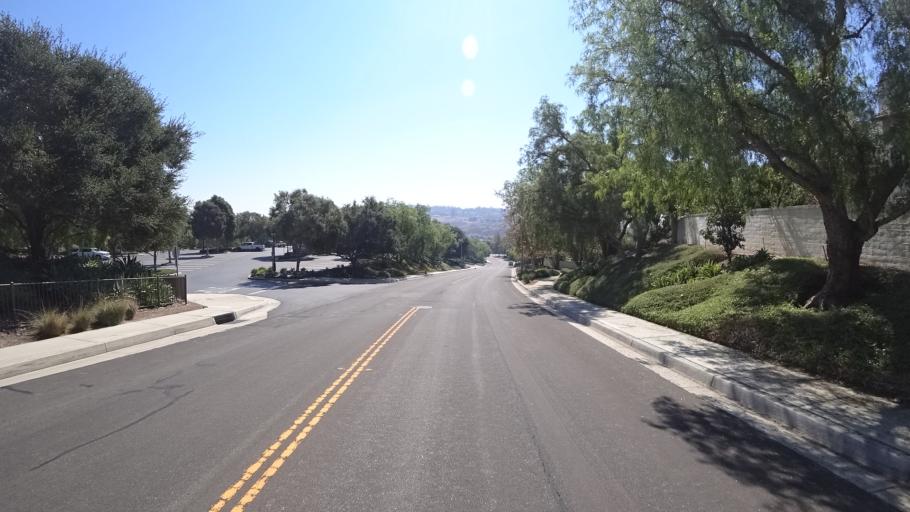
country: US
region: California
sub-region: Orange County
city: San Clemente
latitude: 33.4644
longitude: -117.5907
